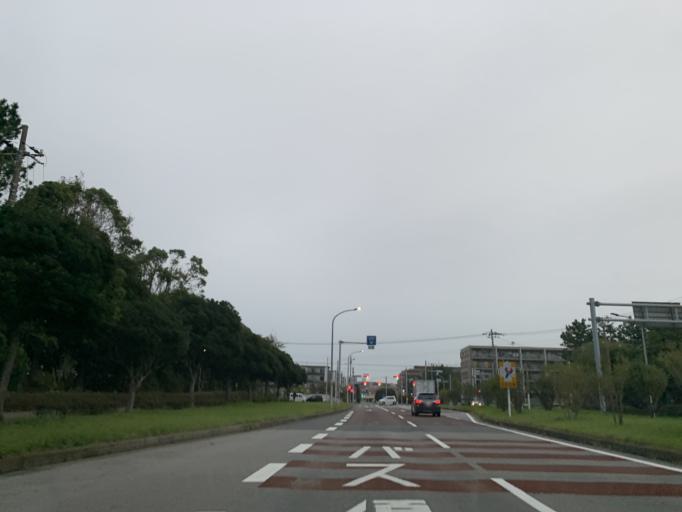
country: JP
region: Chiba
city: Funabashi
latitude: 35.6625
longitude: 140.0352
